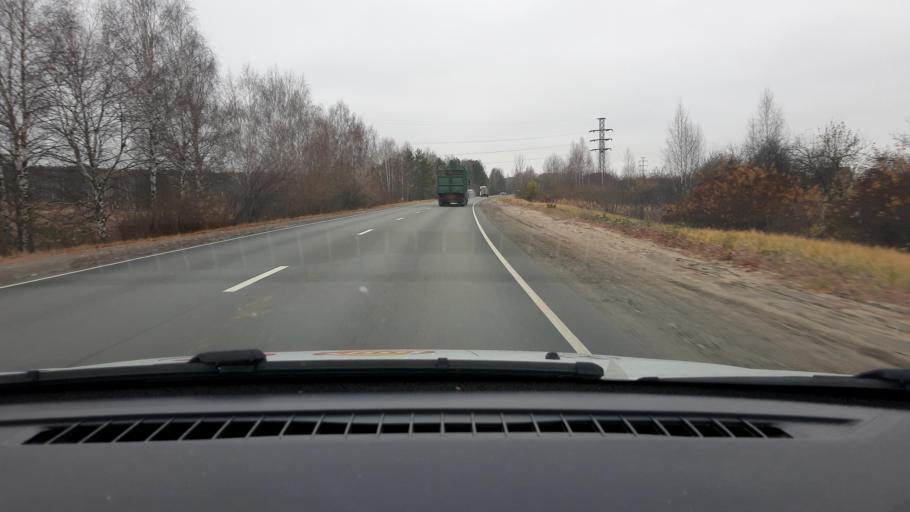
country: RU
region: Nizjnij Novgorod
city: Gidrotorf
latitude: 56.5566
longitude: 43.5045
